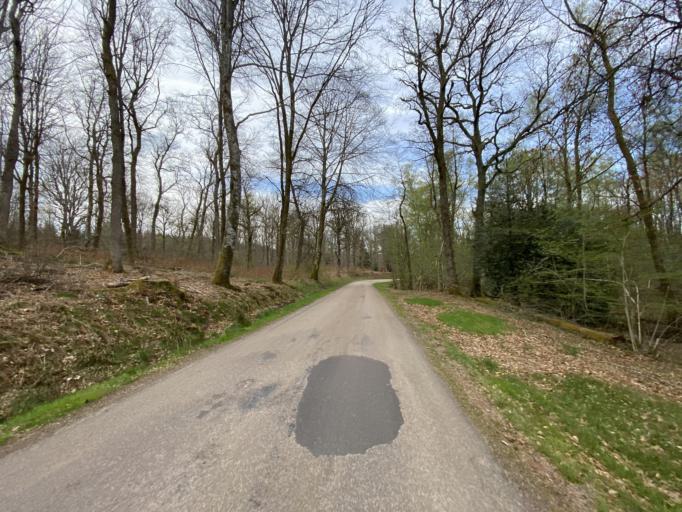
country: FR
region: Bourgogne
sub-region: Departement de la Cote-d'Or
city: Saulieu
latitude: 47.3044
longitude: 4.0881
